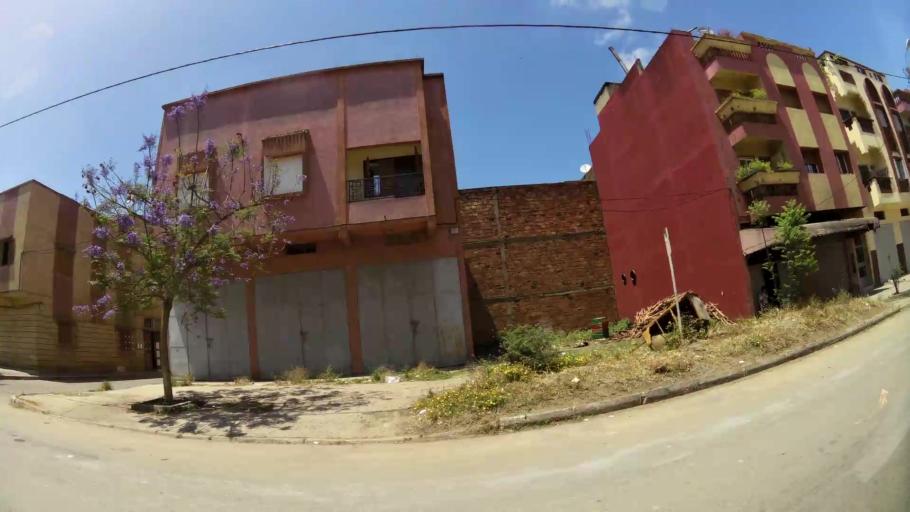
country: MA
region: Gharb-Chrarda-Beni Hssen
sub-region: Kenitra Province
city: Kenitra
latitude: 34.2603
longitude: -6.5531
